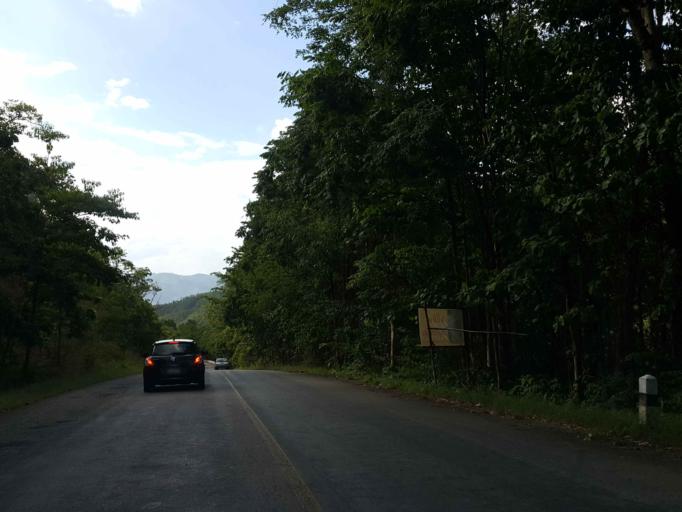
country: TH
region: Lampang
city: Thoen
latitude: 17.6235
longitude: 99.3135
